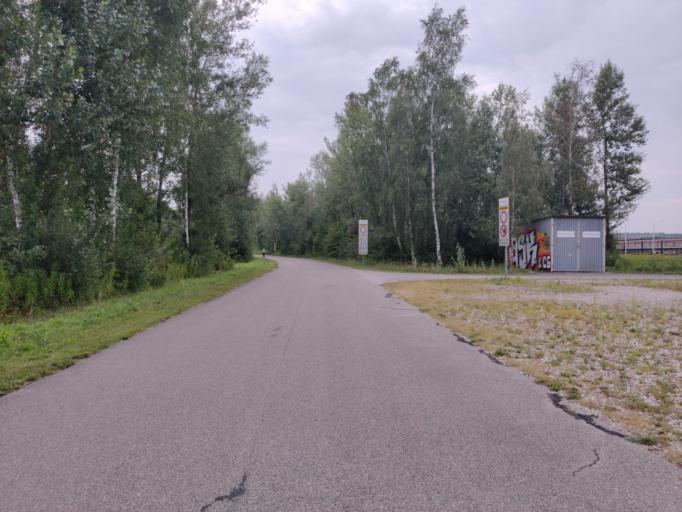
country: AT
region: Upper Austria
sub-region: Politischer Bezirk Linz-Land
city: Asten
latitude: 48.2518
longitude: 14.4300
